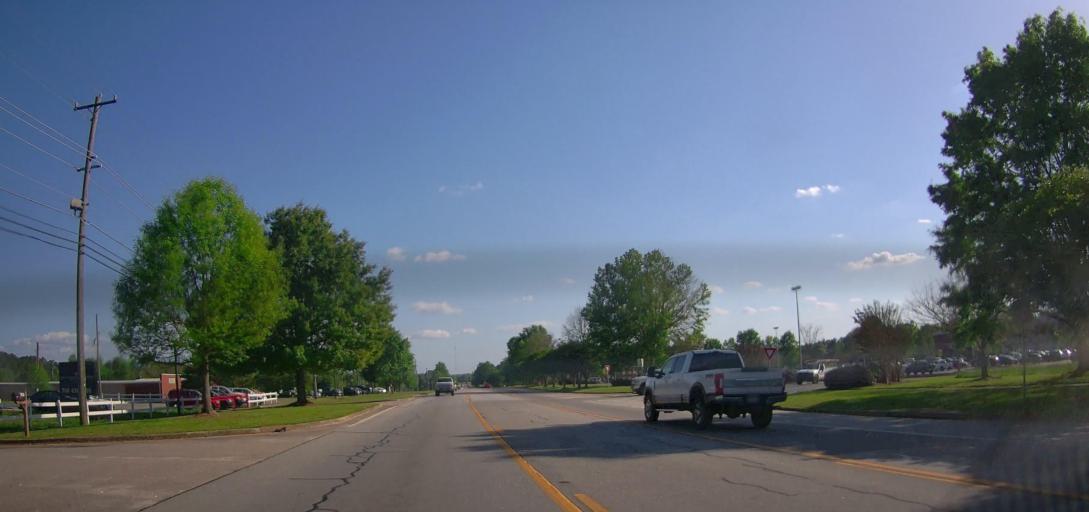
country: US
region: Georgia
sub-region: Morgan County
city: Madison
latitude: 33.5746
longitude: -83.4770
